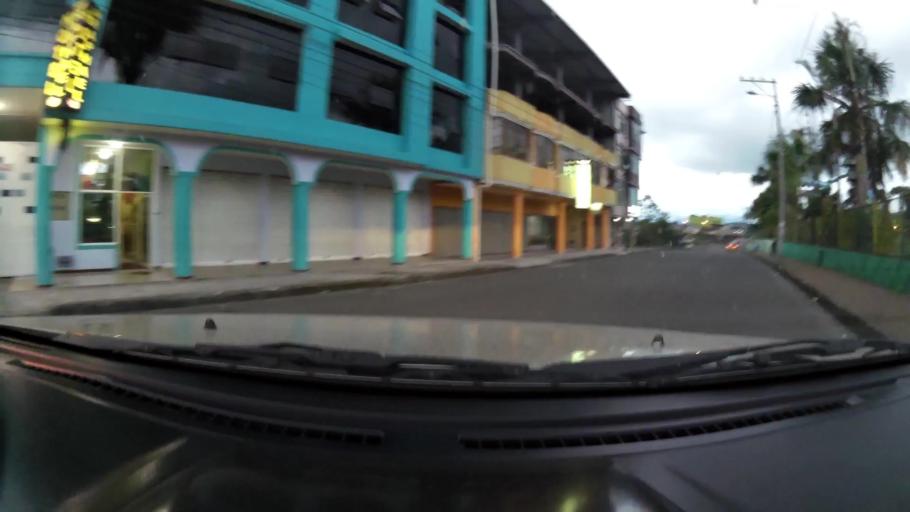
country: EC
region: Pastaza
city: Puyo
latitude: -1.4886
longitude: -78.0048
